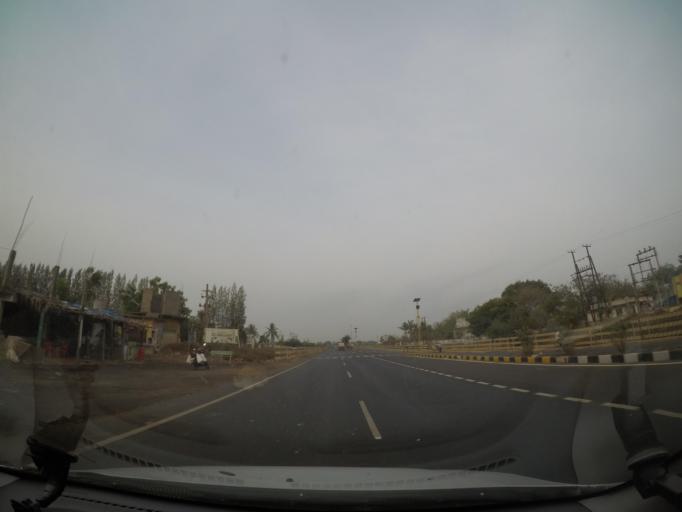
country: IN
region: Andhra Pradesh
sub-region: Krishna
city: Gannavaram
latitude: 16.6028
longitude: 80.8995
